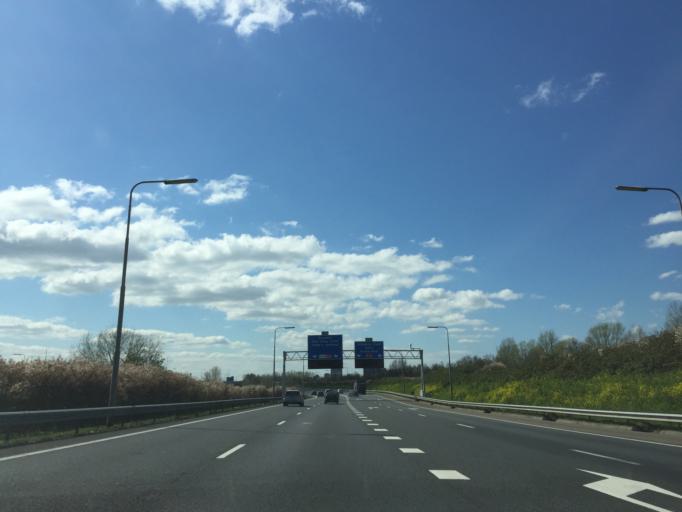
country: NL
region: South Holland
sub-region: Gemeente Den Haag
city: Ypenburg
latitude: 52.0576
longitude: 4.3689
